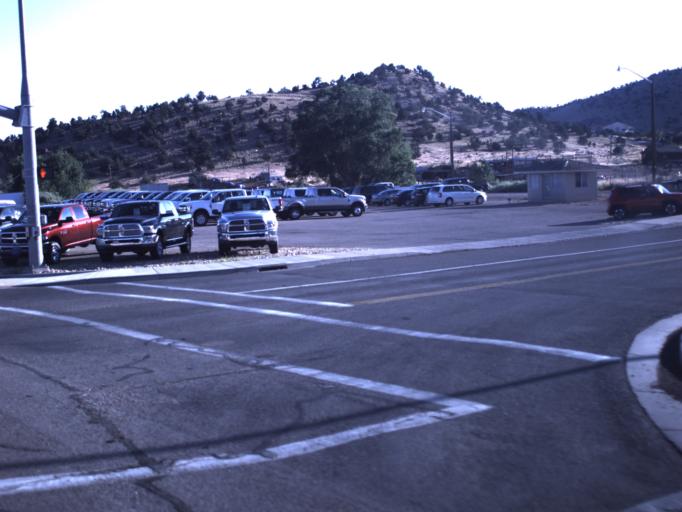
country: US
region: Utah
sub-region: Iron County
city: Cedar City
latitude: 37.6951
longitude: -113.0627
